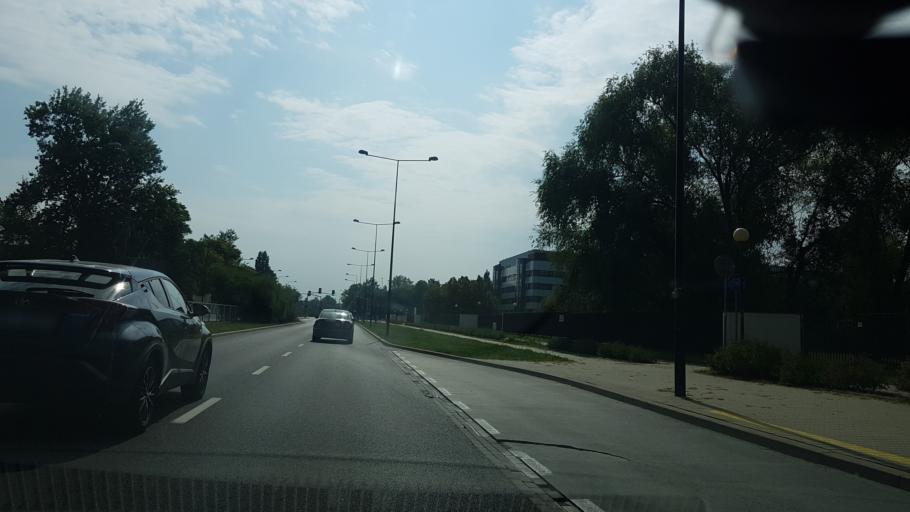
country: PL
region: Masovian Voivodeship
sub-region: Warszawa
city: Ursynow
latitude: 52.1645
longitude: 21.0458
